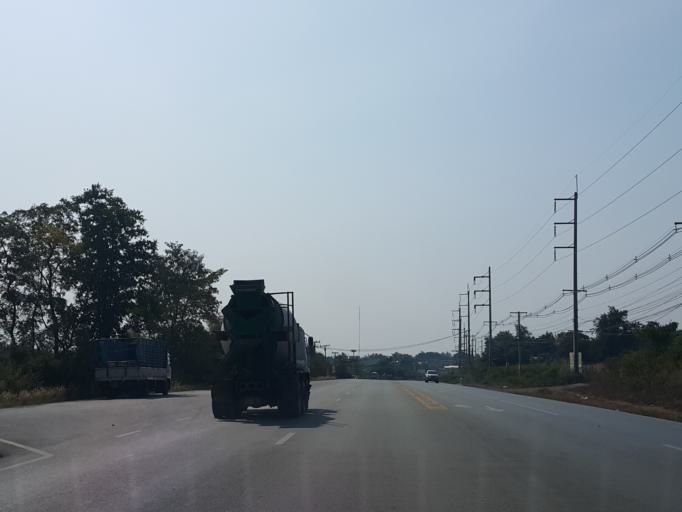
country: TH
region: Chiang Mai
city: Chom Thong
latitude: 18.3658
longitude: 98.6802
